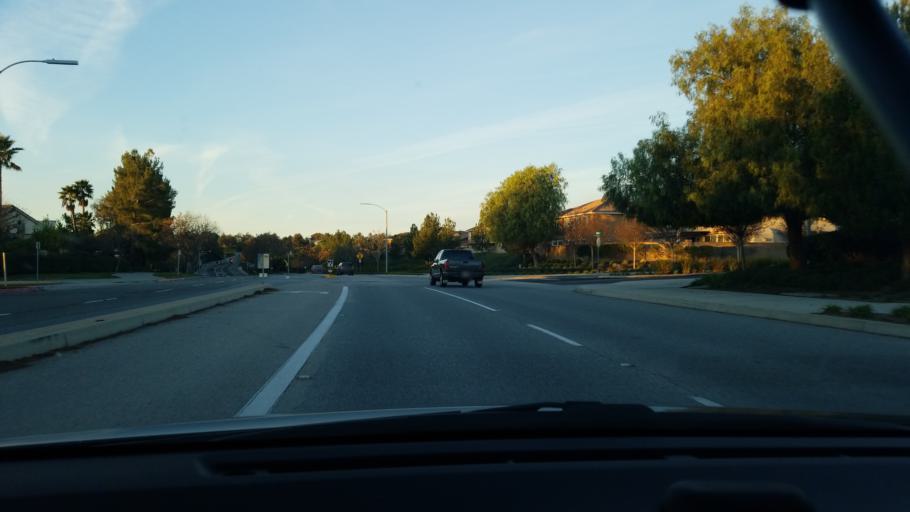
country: US
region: California
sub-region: Riverside County
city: Temecula
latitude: 33.5039
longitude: -117.0953
